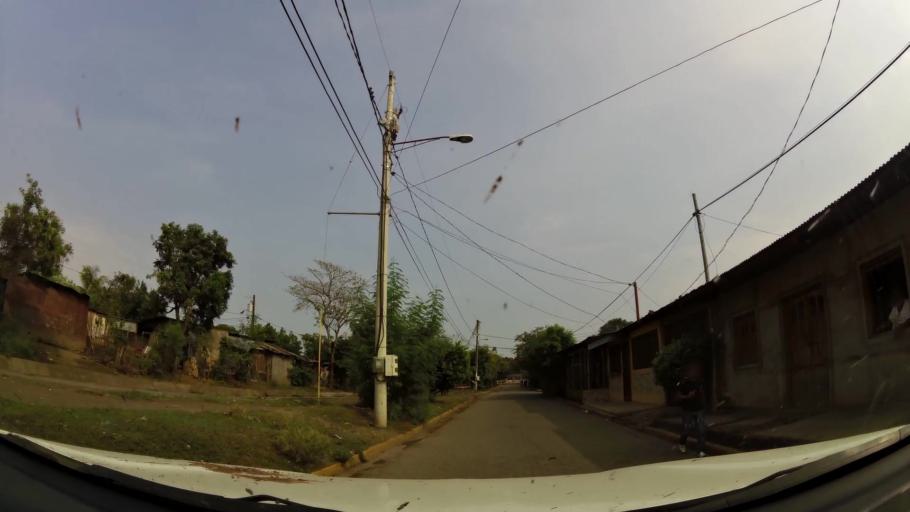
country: NI
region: Masaya
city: Masaya
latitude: 11.9700
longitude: -86.0860
